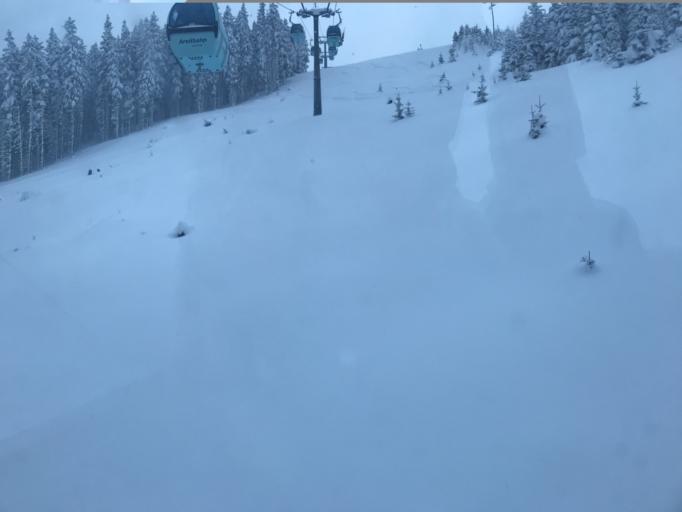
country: AT
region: Salzburg
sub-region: Politischer Bezirk Zell am See
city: Kaprun
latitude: 47.3136
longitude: 12.7538
